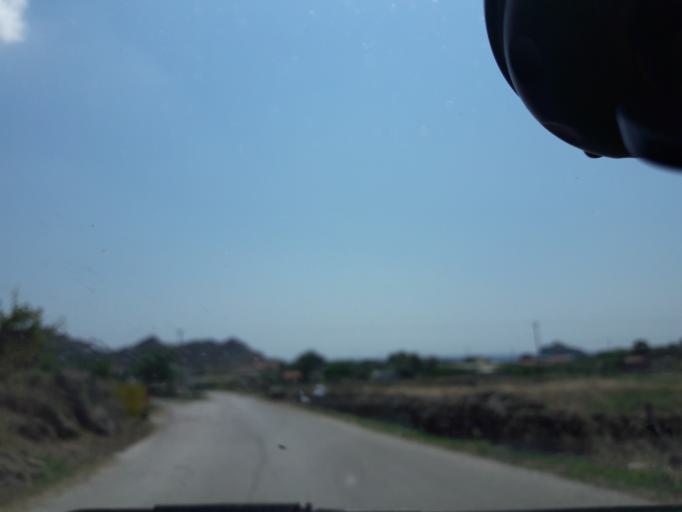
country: GR
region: North Aegean
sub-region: Nomos Lesvou
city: Myrina
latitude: 39.8445
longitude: 25.0841
